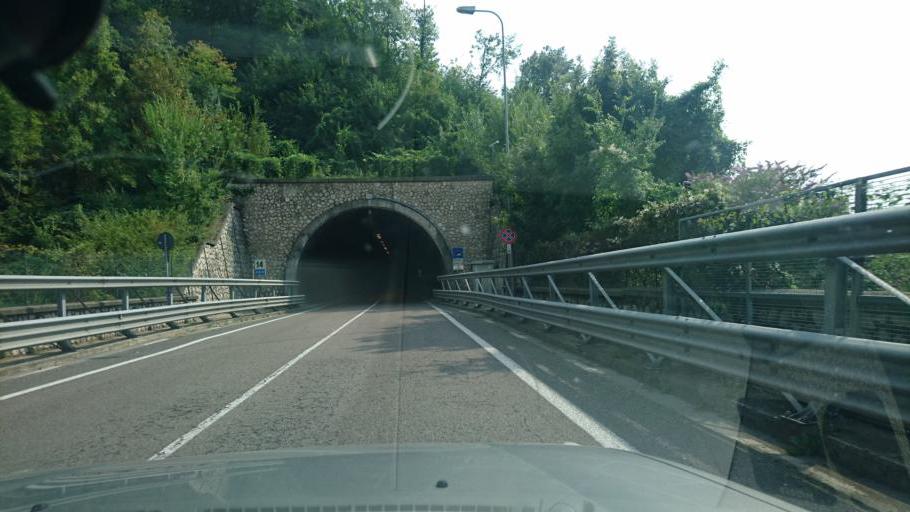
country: IT
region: Lombardy
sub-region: Provincia di Brescia
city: Barghe
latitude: 45.6785
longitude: 10.4114
